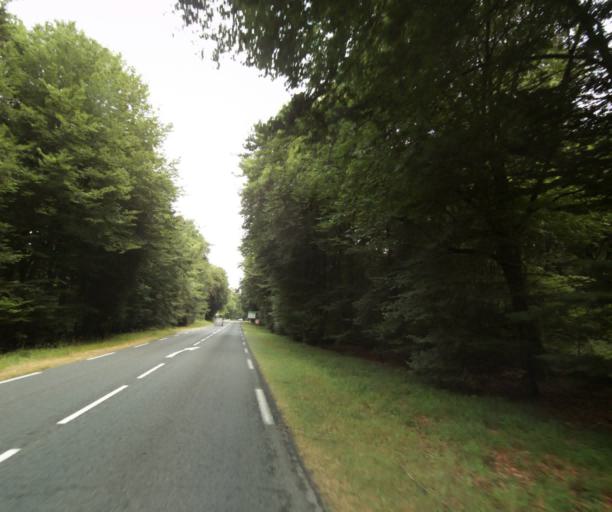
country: FR
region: Ile-de-France
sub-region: Departement de Seine-et-Marne
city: Barbizon
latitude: 48.4138
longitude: 2.6411
